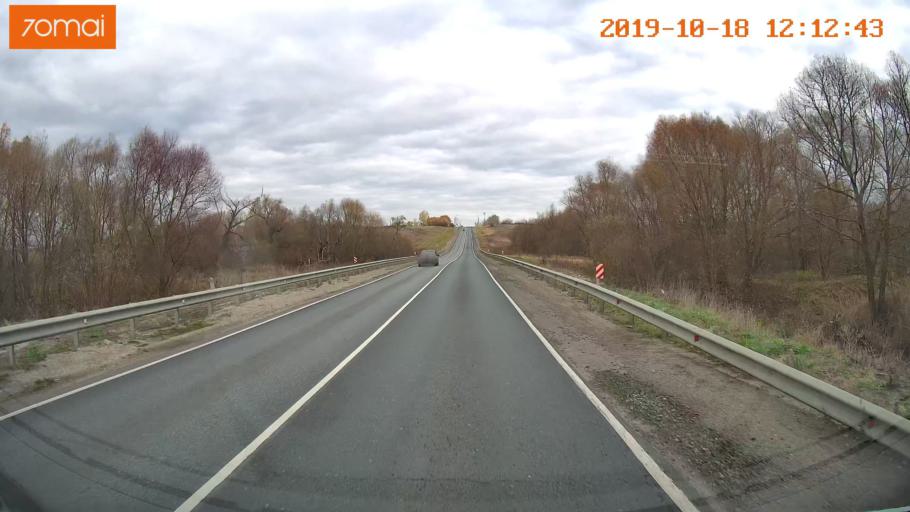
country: RU
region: Rjazan
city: Zakharovo
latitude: 54.4145
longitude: 39.3614
